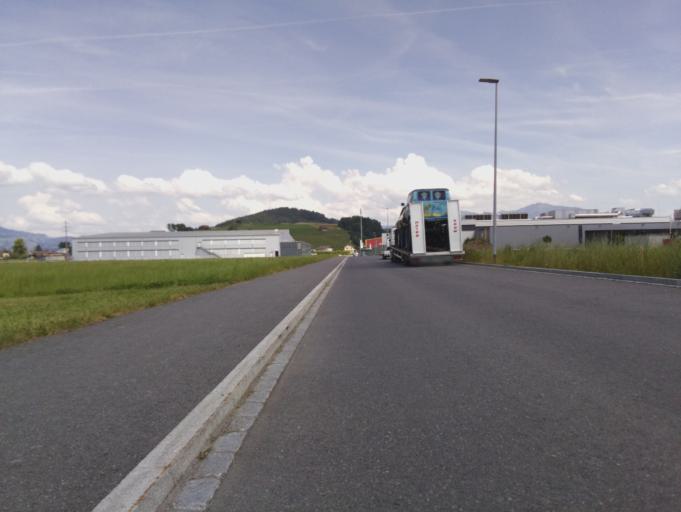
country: CH
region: Schwyz
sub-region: Bezirk March
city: Lachen
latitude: 47.1956
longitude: 8.8759
